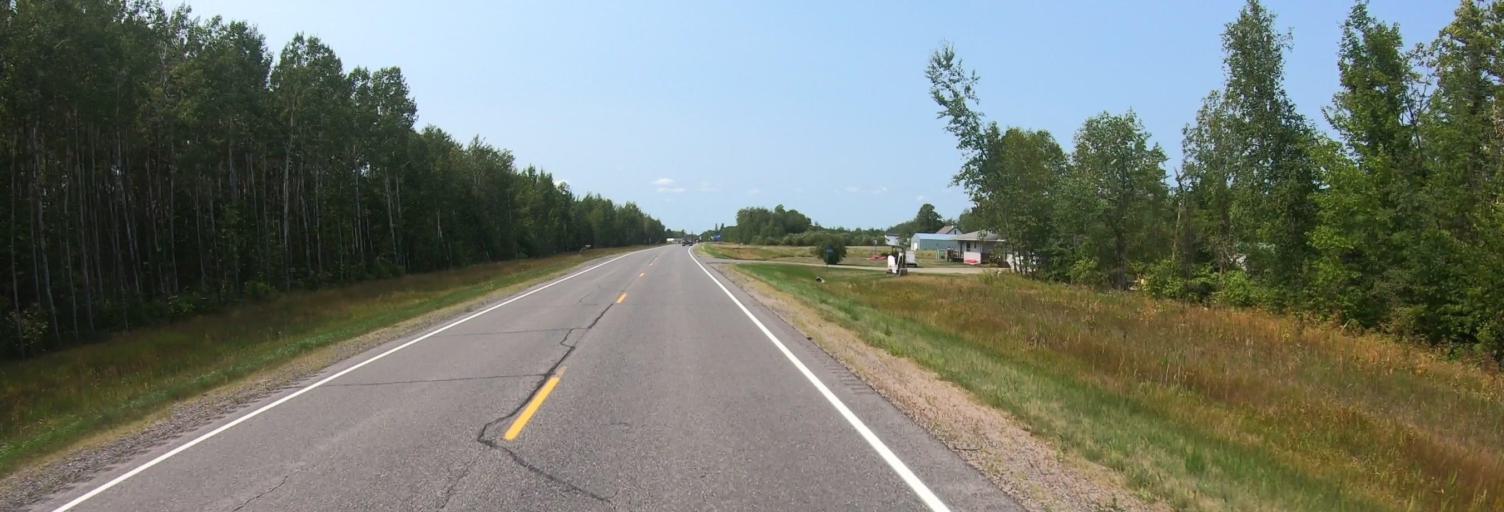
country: US
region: Minnesota
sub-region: Koochiching County
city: International Falls
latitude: 48.5126
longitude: -93.7848
